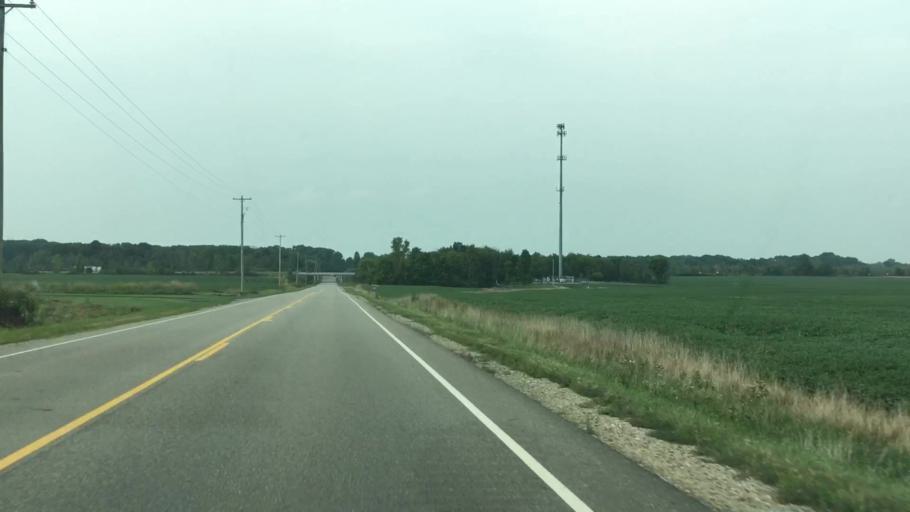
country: US
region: Michigan
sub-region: Ottawa County
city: Hudsonville
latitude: 42.8303
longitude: -85.9006
